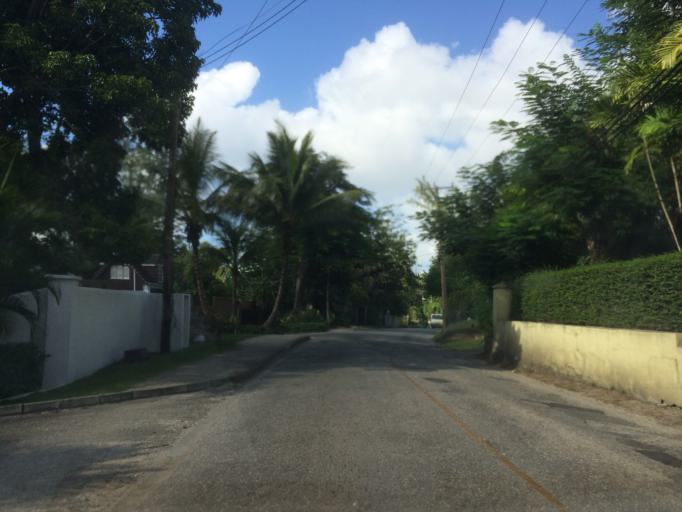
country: BB
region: Saint Peter
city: Speightstown
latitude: 13.2283
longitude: -59.6421
